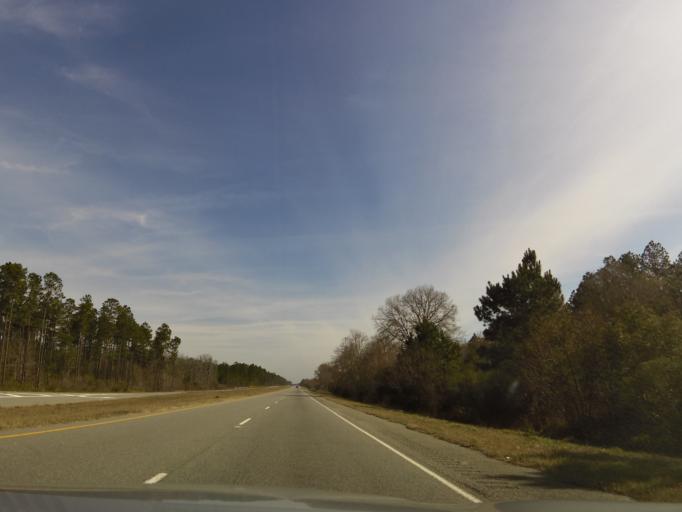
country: US
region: Georgia
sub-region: Lanier County
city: Lakeland
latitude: 30.9597
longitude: -82.9459
